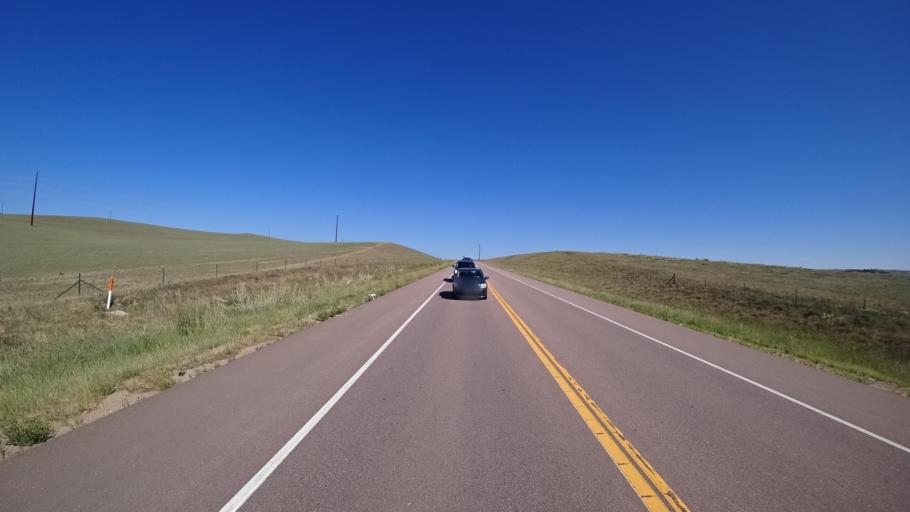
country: US
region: Colorado
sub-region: El Paso County
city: Cimarron Hills
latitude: 38.7992
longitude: -104.6606
